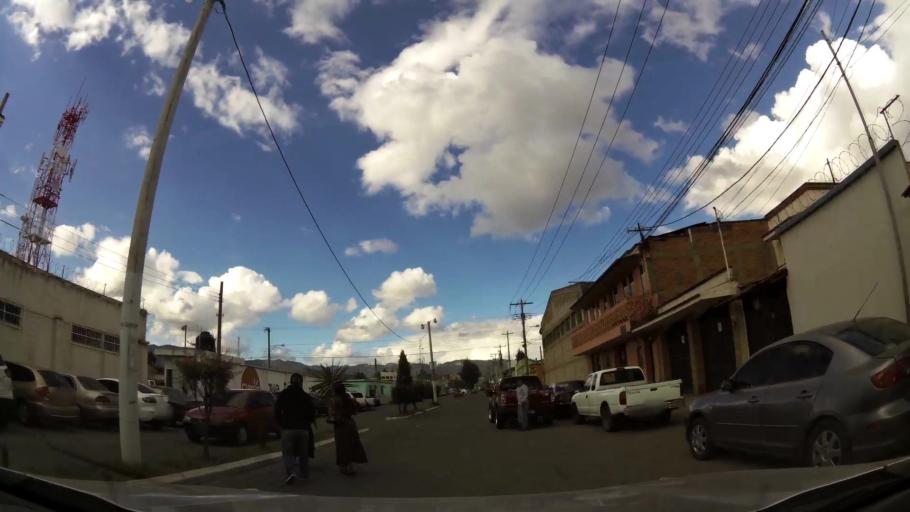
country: GT
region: Quetzaltenango
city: Quetzaltenango
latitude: 14.8472
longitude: -91.5257
